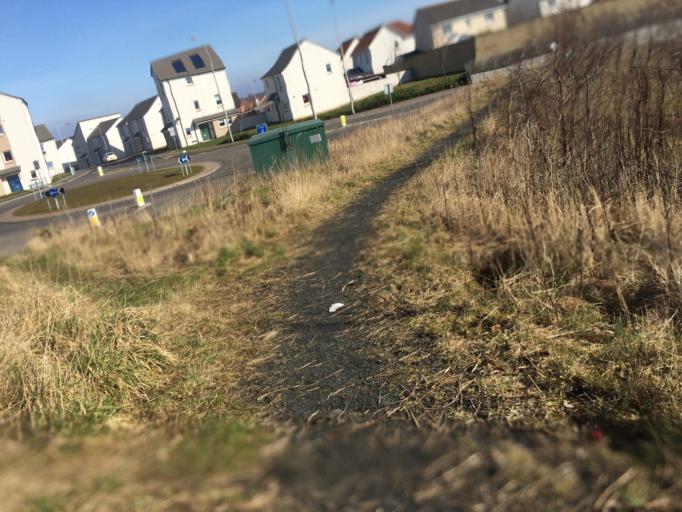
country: GB
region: Scotland
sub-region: Fife
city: Kirkcaldy
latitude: 56.1364
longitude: -3.1952
